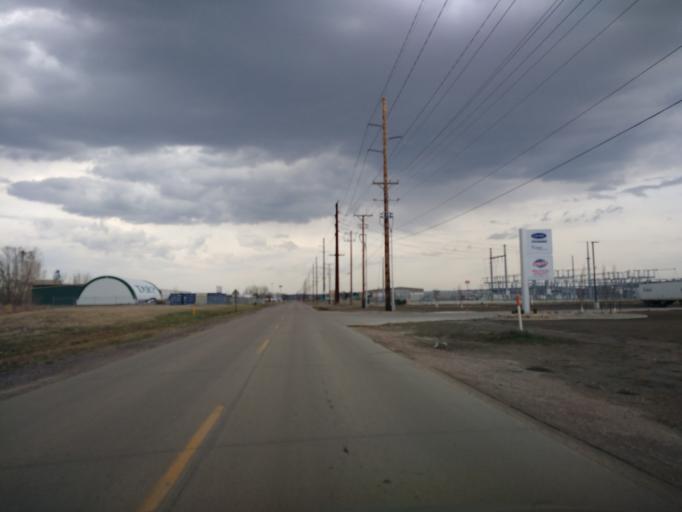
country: US
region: Iowa
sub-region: Woodbury County
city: Sergeant Bluff
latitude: 42.4157
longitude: -96.3700
